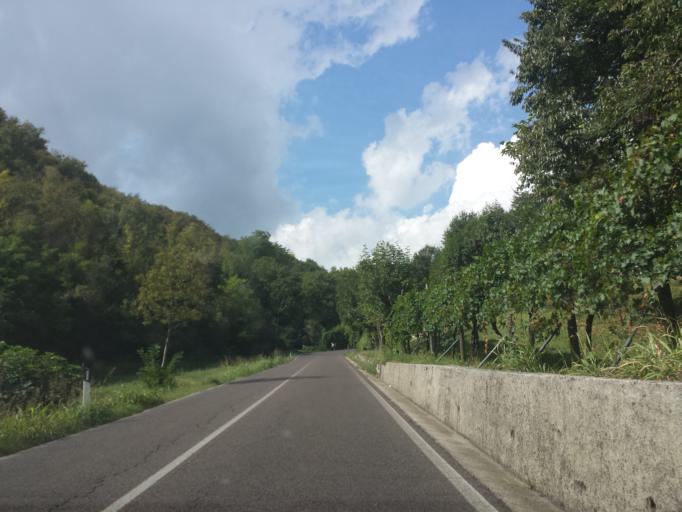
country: IT
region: Veneto
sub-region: Provincia di Vicenza
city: Castelgomberto
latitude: 45.5851
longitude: 11.4059
